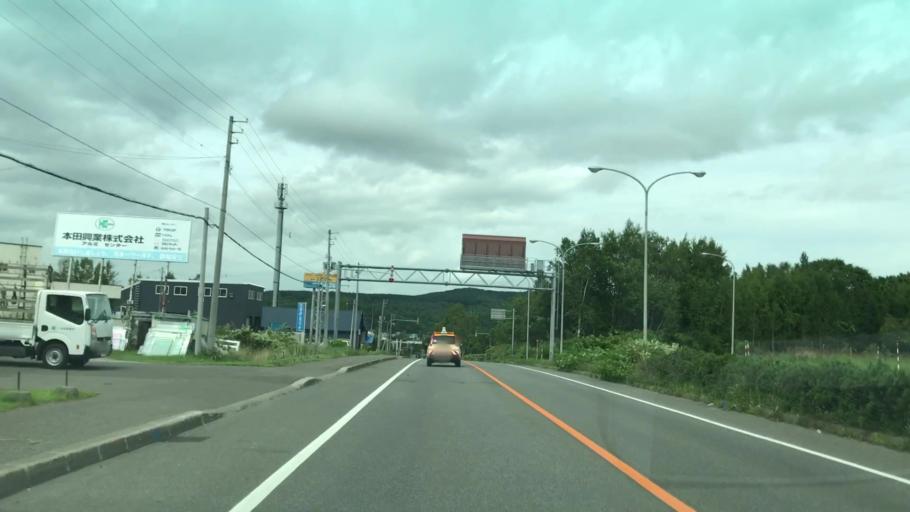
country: JP
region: Hokkaido
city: Niseko Town
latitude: 42.9150
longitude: 140.7498
